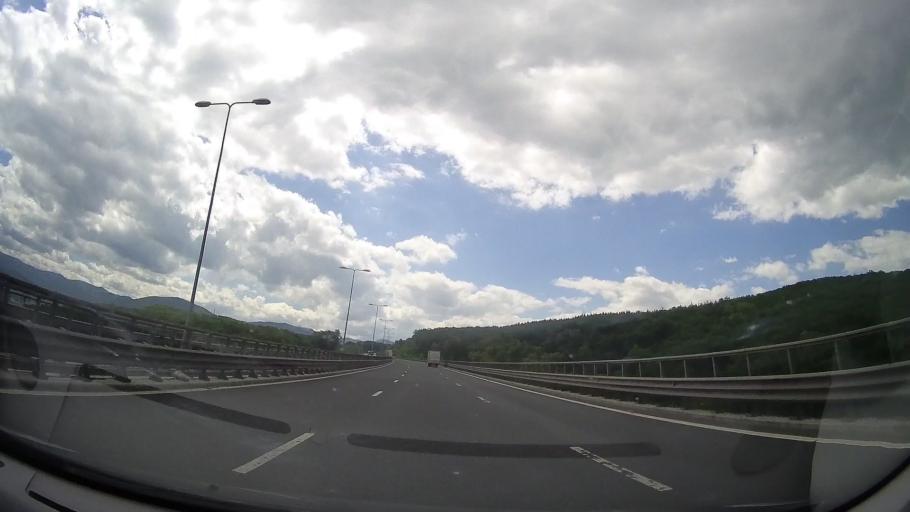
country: RO
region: Sibiu
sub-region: Comuna Orlat
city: Orlat
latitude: 45.7837
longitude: 23.9738
